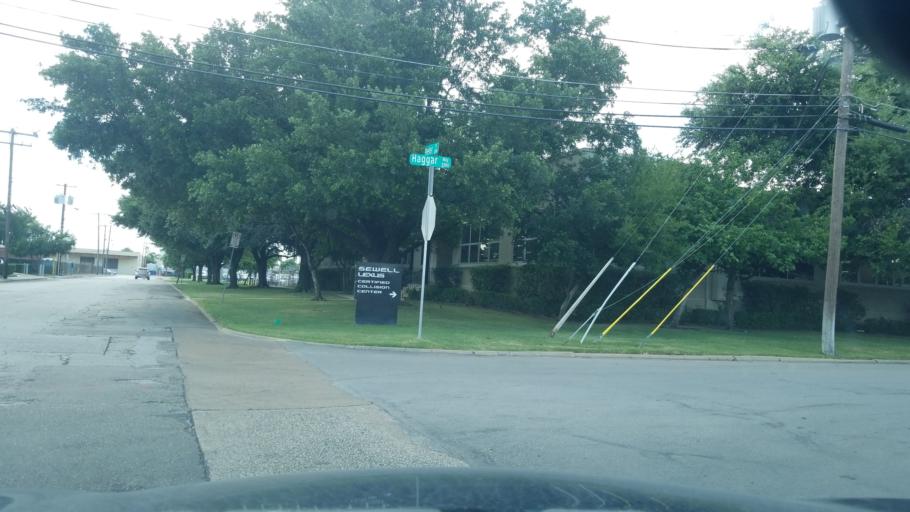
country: US
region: Texas
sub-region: Dallas County
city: University Park
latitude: 32.8311
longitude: -96.8326
